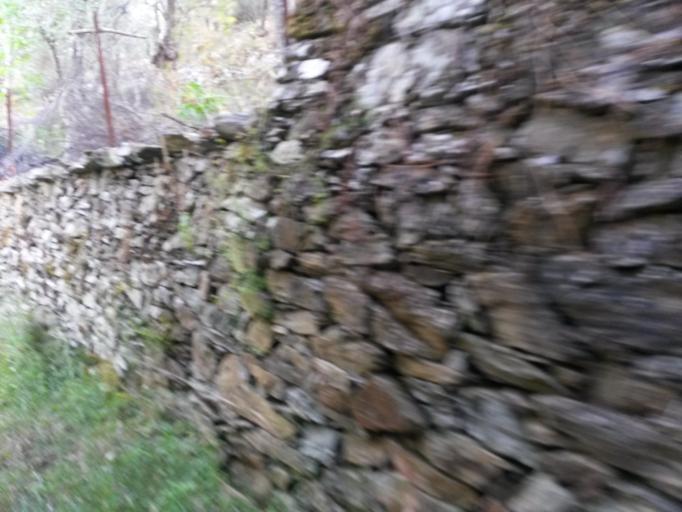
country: GR
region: North Aegean
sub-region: Nomos Lesvou
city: Agiasos
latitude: 39.1104
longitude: 26.3933
